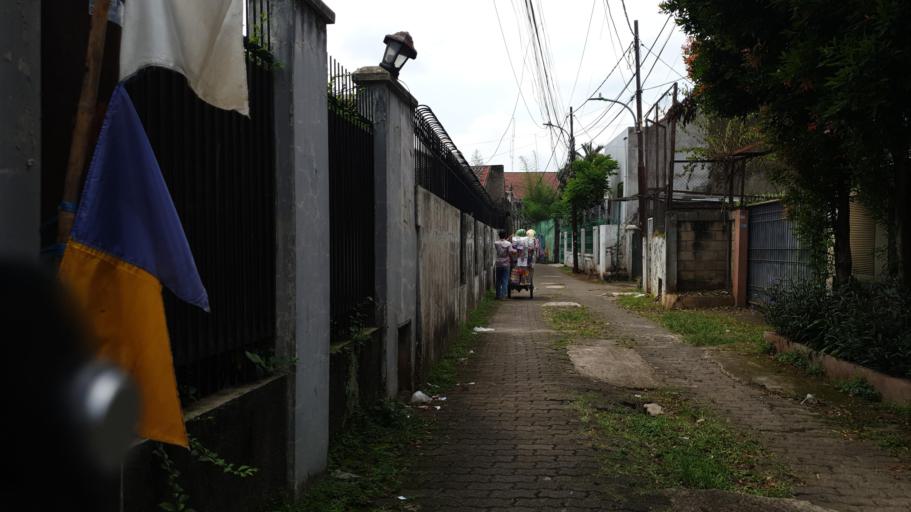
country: ID
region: Banten
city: South Tangerang
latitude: -6.2816
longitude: 106.7931
